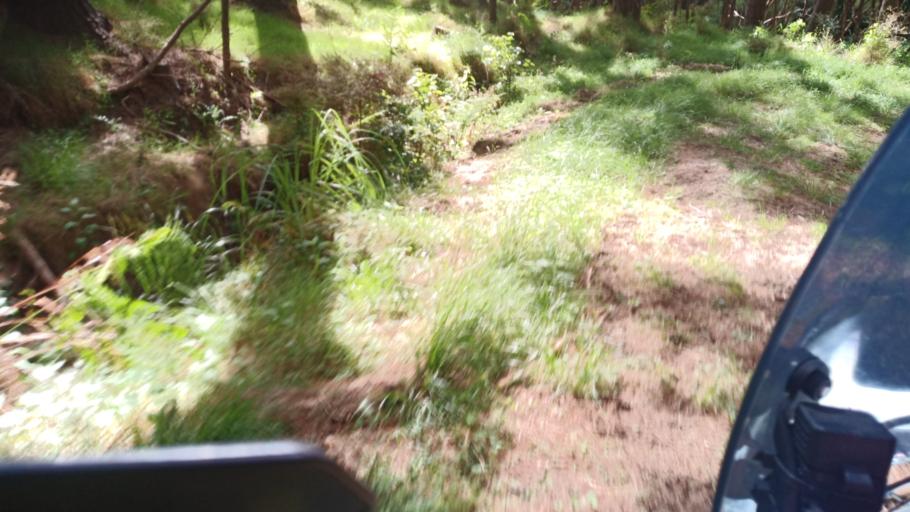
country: NZ
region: Gisborne
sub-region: Gisborne District
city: Gisborne
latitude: -38.4585
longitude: 177.9246
